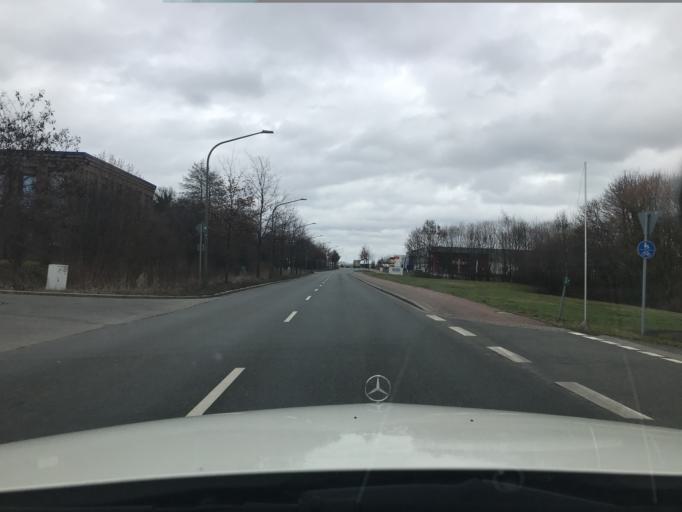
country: DE
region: North Rhine-Westphalia
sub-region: Regierungsbezirk Arnsberg
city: Hamm
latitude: 51.6177
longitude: 7.8512
